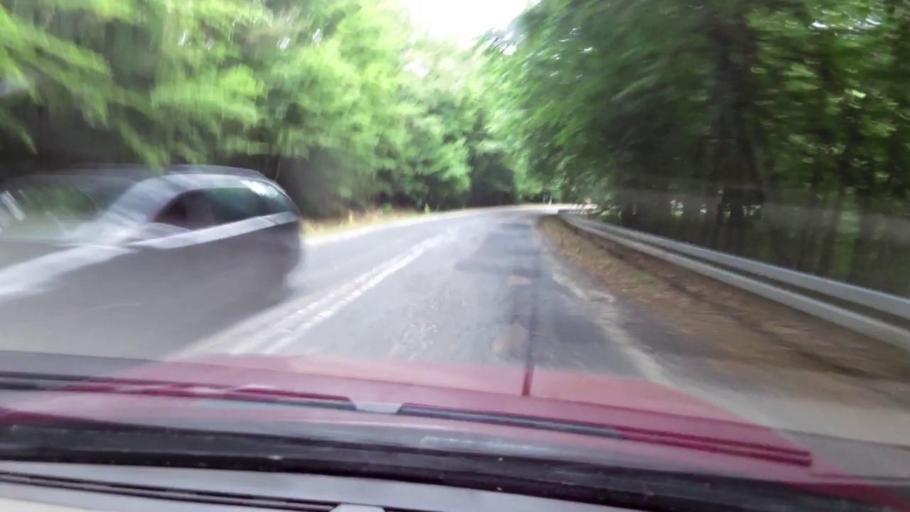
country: PL
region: Pomeranian Voivodeship
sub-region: Powiat bytowski
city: Trzebielino
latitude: 54.2682
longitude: 17.0121
